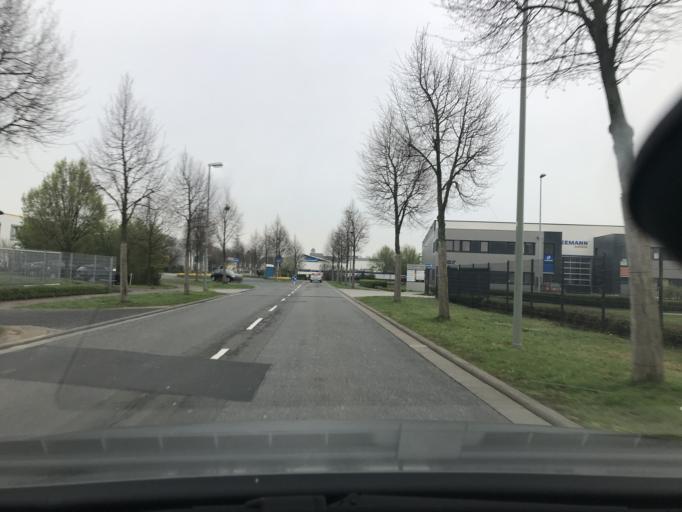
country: DE
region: North Rhine-Westphalia
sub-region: Regierungsbezirk Dusseldorf
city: Krefeld
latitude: 51.3713
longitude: 6.6385
